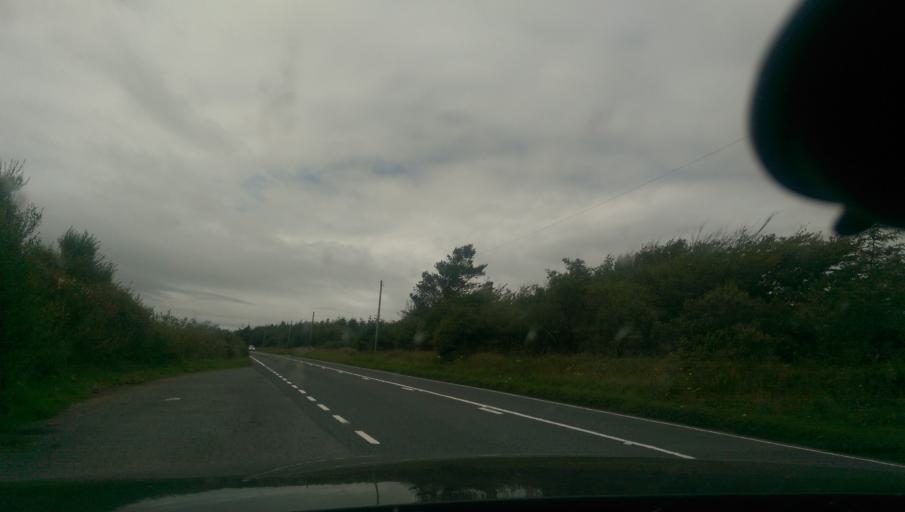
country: GB
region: England
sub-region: Cornwall
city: Jacobstow
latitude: 50.6580
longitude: -4.5605
